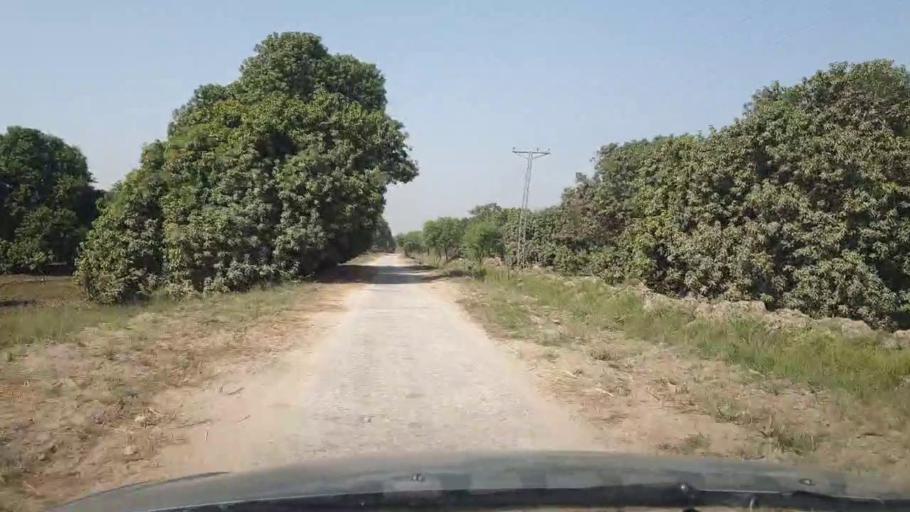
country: PK
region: Sindh
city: Tando Jam
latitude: 25.3637
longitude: 68.5109
